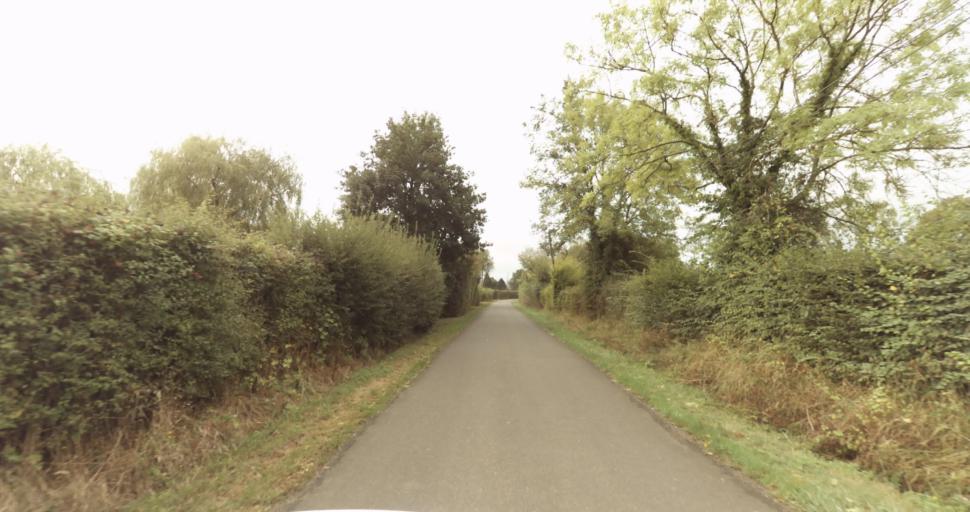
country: FR
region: Lower Normandy
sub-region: Departement du Calvados
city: Livarot
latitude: 48.9328
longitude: 0.1094
